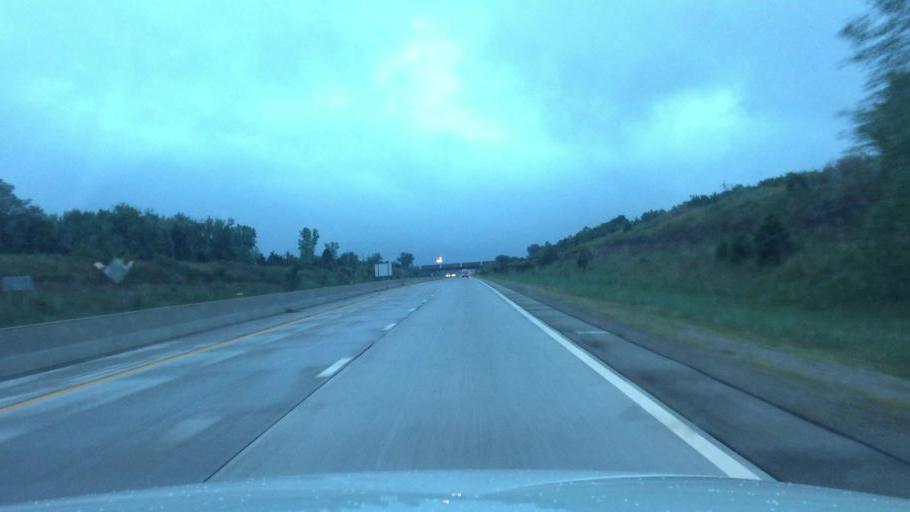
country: US
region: Kansas
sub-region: Neosho County
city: Chanute
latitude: 37.6688
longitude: -95.4796
